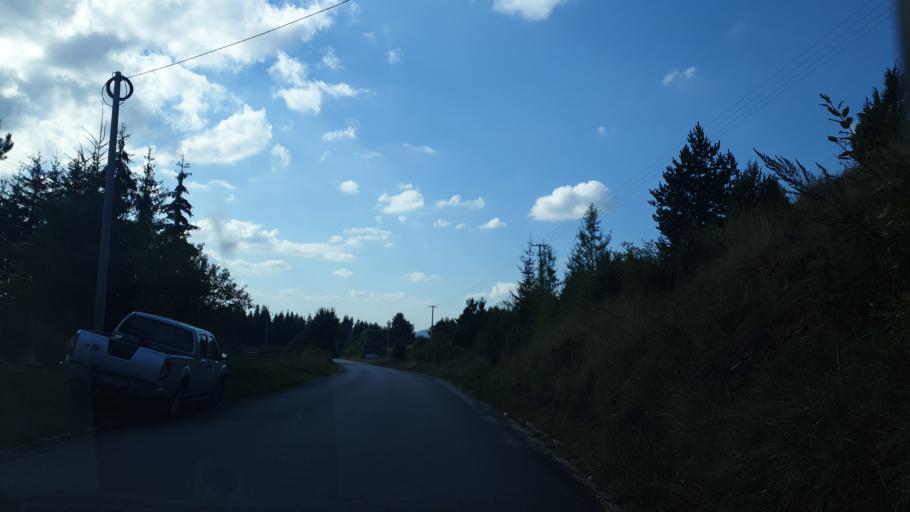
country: RS
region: Central Serbia
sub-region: Zlatiborski Okrug
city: Nova Varos
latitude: 43.4296
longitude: 19.8935
